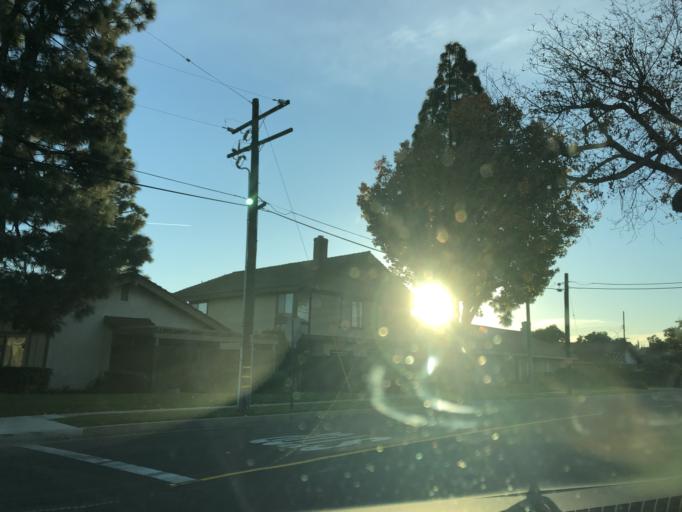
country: US
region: California
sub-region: Orange County
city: Tustin
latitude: 33.7529
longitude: -117.8439
